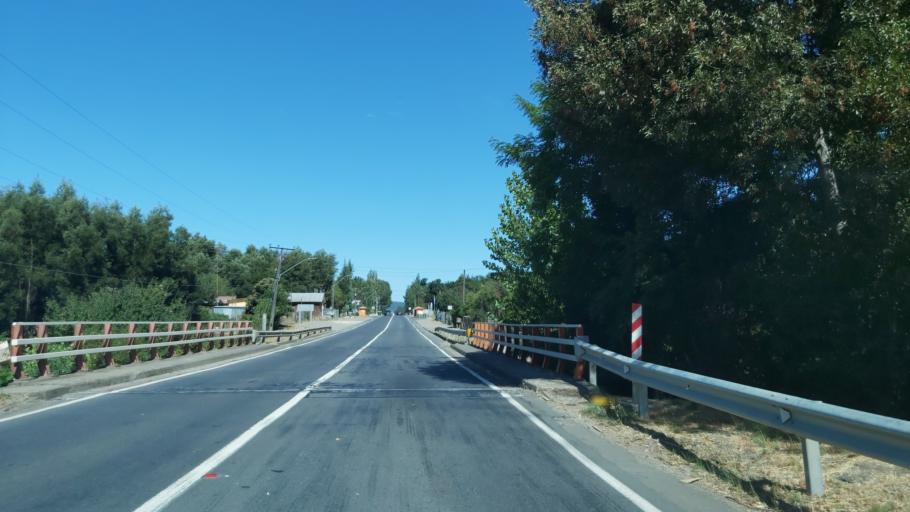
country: CL
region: Biobio
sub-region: Provincia de Concepcion
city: Lota
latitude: -37.1517
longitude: -72.9763
